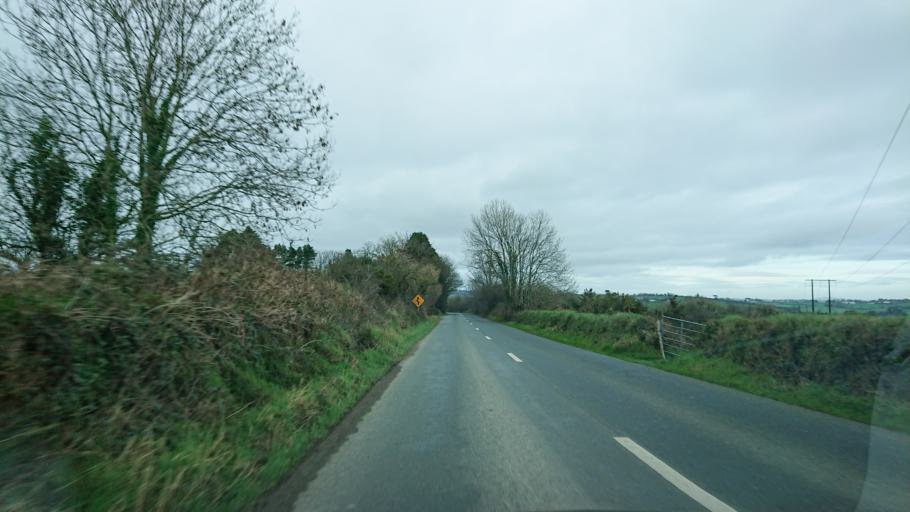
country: IE
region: Leinster
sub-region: Kilkenny
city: Mooncoin
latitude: 52.2104
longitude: -7.2457
